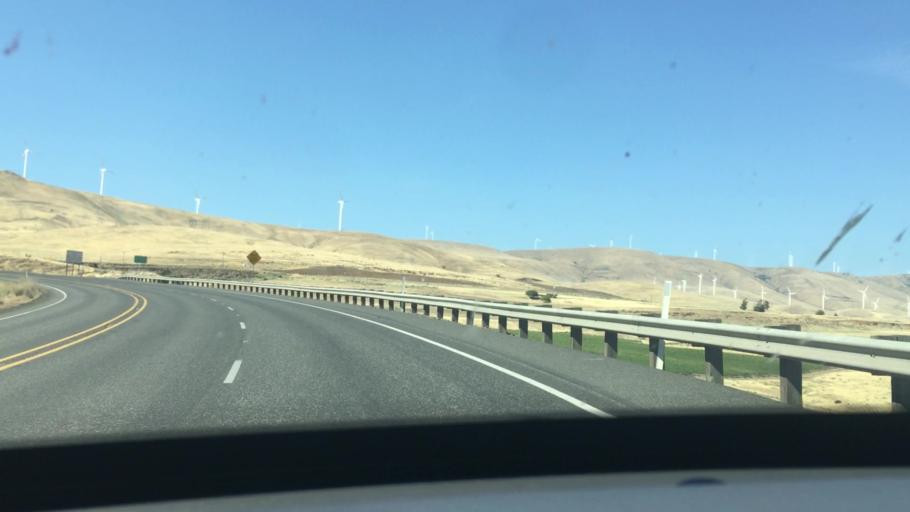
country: US
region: Washington
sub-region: Klickitat County
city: Goldendale
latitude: 45.6924
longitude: -120.8173
